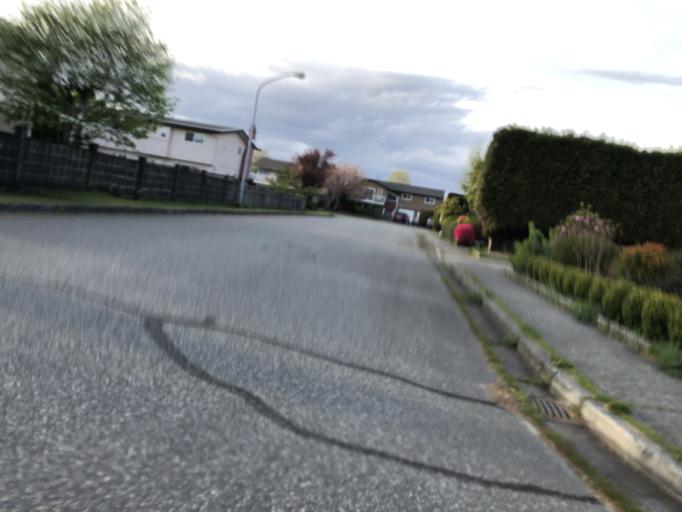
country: CA
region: British Columbia
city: Richmond
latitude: 49.1432
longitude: -123.1042
